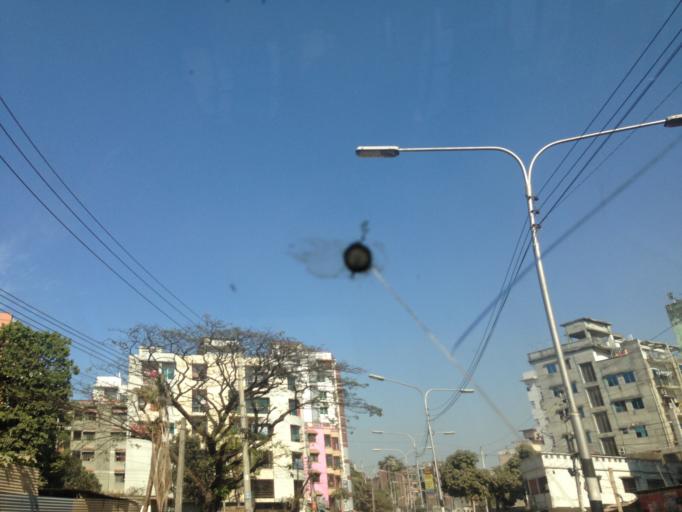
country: BD
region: Dhaka
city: Azimpur
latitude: 23.8134
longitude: 90.3618
